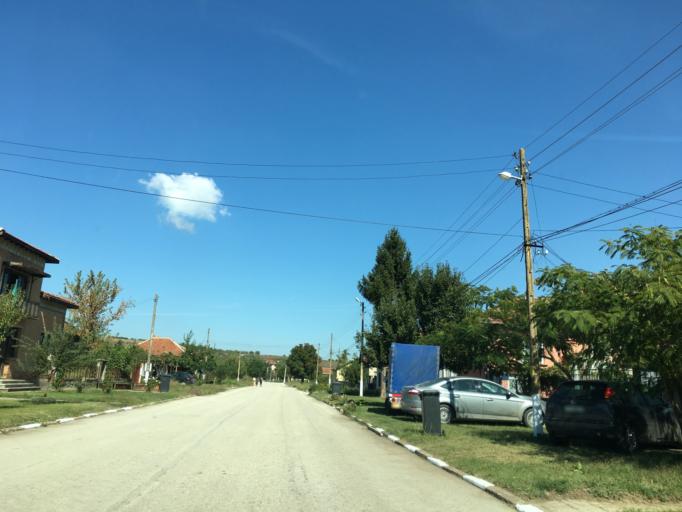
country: RO
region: Olt
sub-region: Comuna Orlea
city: Orlea
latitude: 43.6426
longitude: 24.3995
